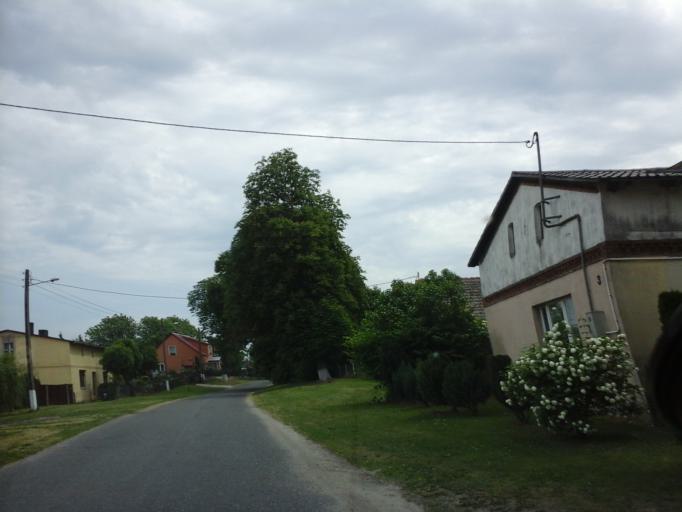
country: PL
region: West Pomeranian Voivodeship
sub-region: Powiat choszczenski
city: Bierzwnik
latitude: 53.1462
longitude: 15.6288
